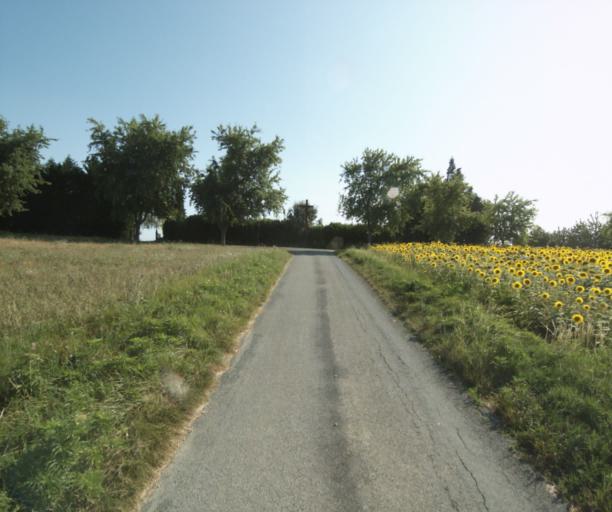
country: FR
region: Midi-Pyrenees
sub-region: Departement de la Haute-Garonne
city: Avignonet-Lauragais
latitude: 43.4278
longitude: 1.8140
